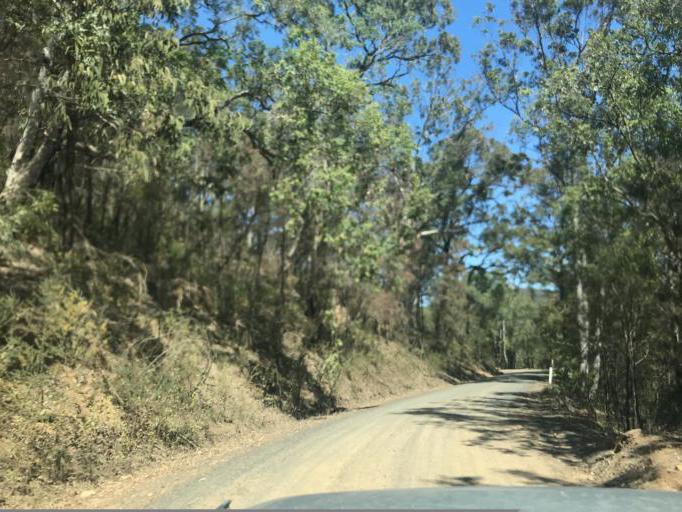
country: AU
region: New South Wales
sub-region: Wyong Shire
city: Little Jilliby
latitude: -33.1582
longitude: 151.0758
